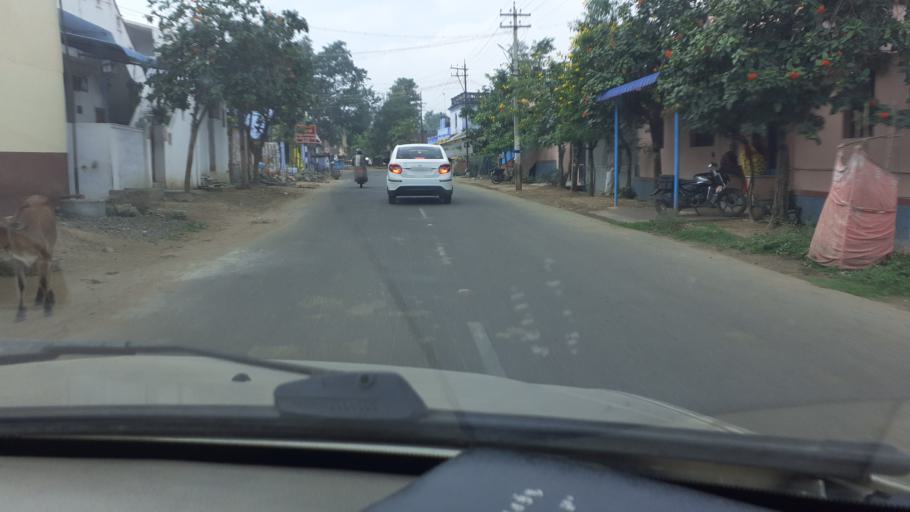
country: IN
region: Tamil Nadu
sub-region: Tirunelveli Kattabo
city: Viravanallur
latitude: 8.7198
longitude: 77.5470
